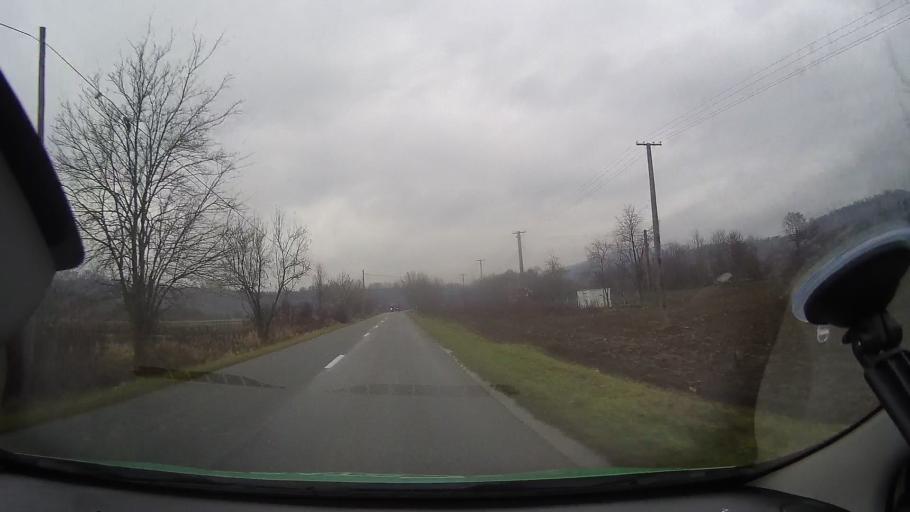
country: RO
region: Arad
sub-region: Comuna Gurahont
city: Gurahont
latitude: 46.2546
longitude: 22.3344
